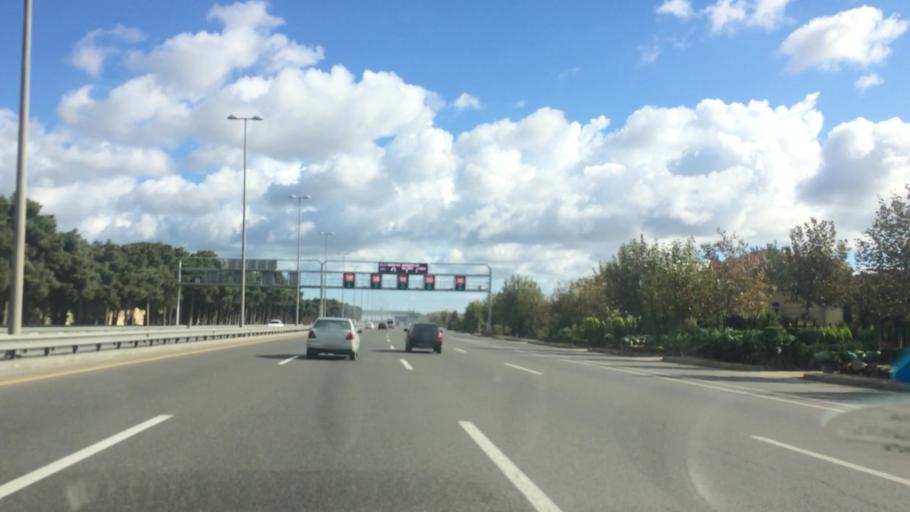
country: AZ
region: Baki
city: Biny Selo
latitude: 40.4636
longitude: 50.0851
